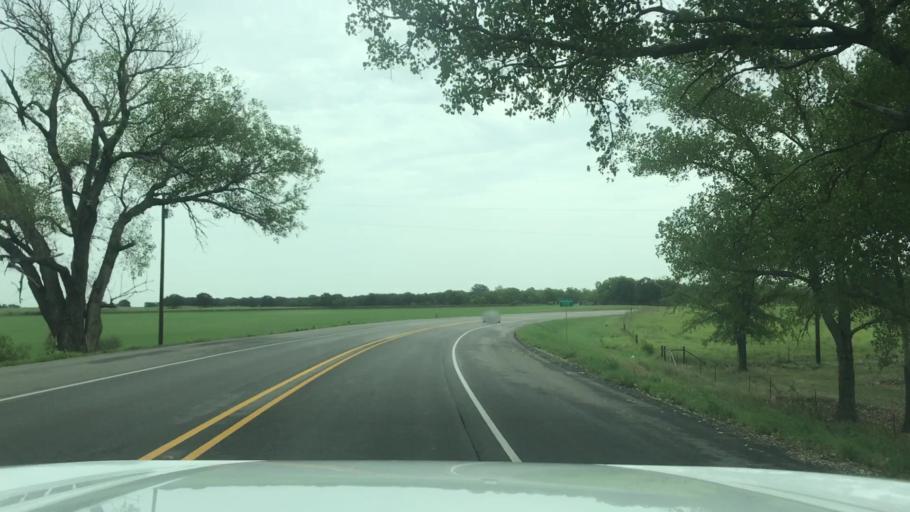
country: US
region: Texas
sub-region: Eastland County
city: Gorman
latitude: 32.2218
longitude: -98.6818
